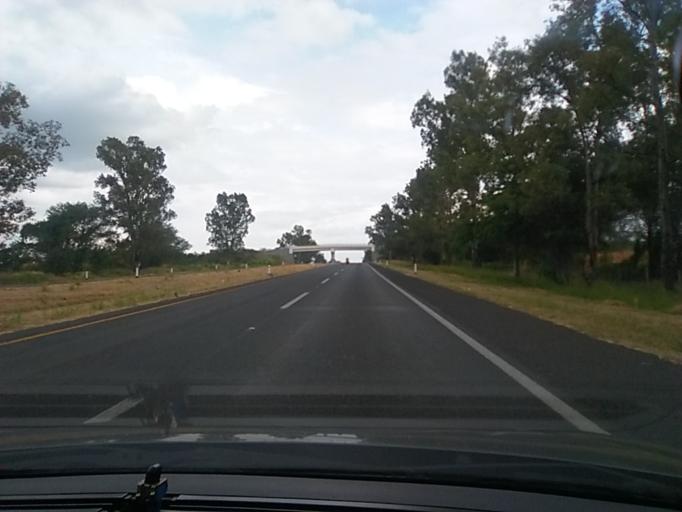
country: MX
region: Jalisco
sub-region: Ocotlan
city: Joconoxtle (La Tuna)
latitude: 20.3700
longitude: -102.6558
